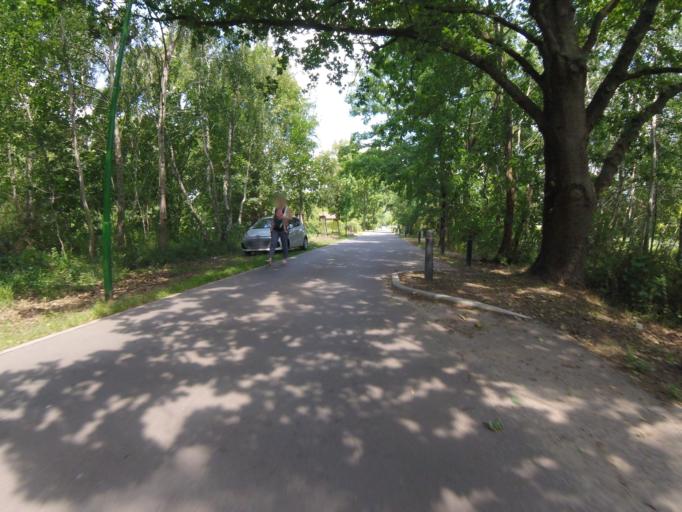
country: DE
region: Brandenburg
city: Bestensee
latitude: 52.2615
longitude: 13.6560
